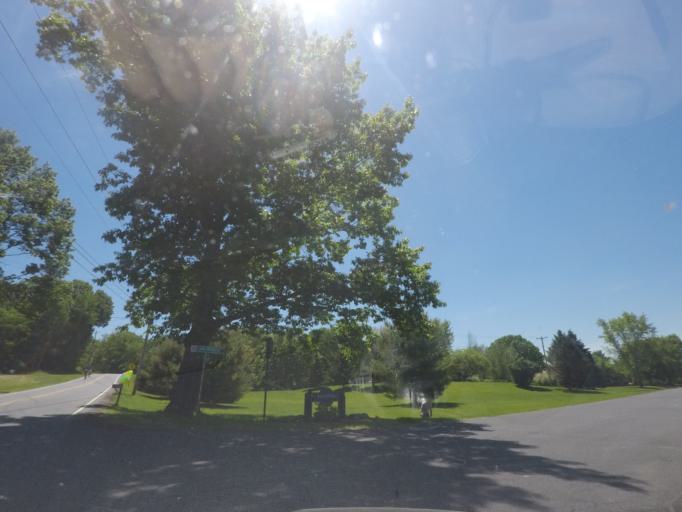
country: US
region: New York
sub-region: Saratoga County
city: Country Knolls
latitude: 42.9442
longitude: -73.7644
